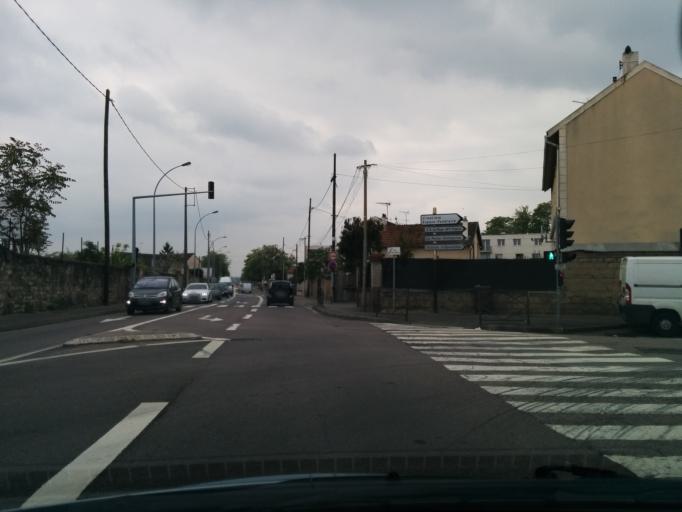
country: FR
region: Ile-de-France
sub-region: Departement des Yvelines
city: Les Mureaux
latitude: 48.9892
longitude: 1.8984
